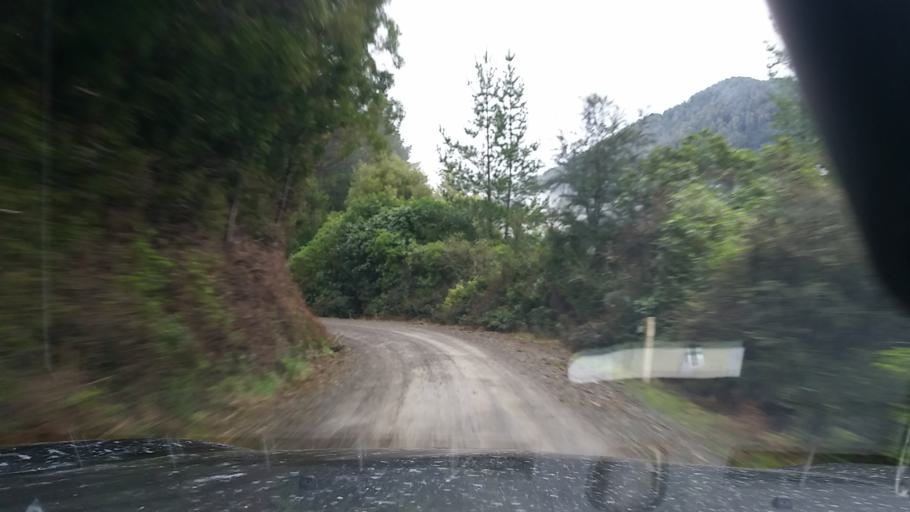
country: NZ
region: Nelson
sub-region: Nelson City
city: Nelson
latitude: -41.3608
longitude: 173.6139
